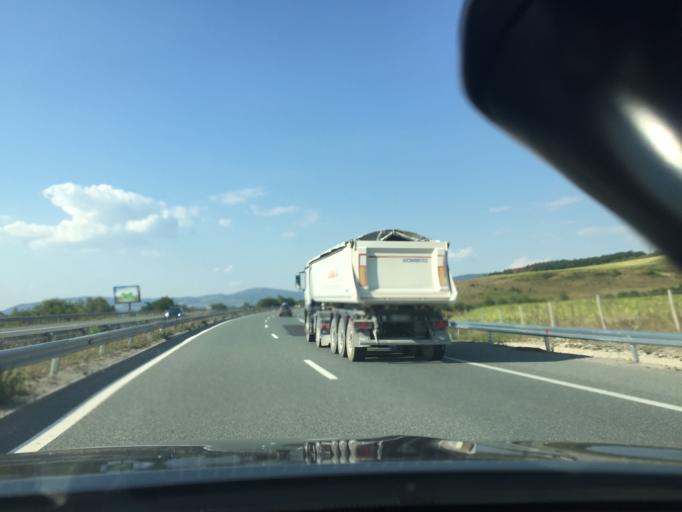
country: BG
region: Pernik
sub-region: Obshtina Pernik
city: Pernik
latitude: 42.5644
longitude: 23.1154
